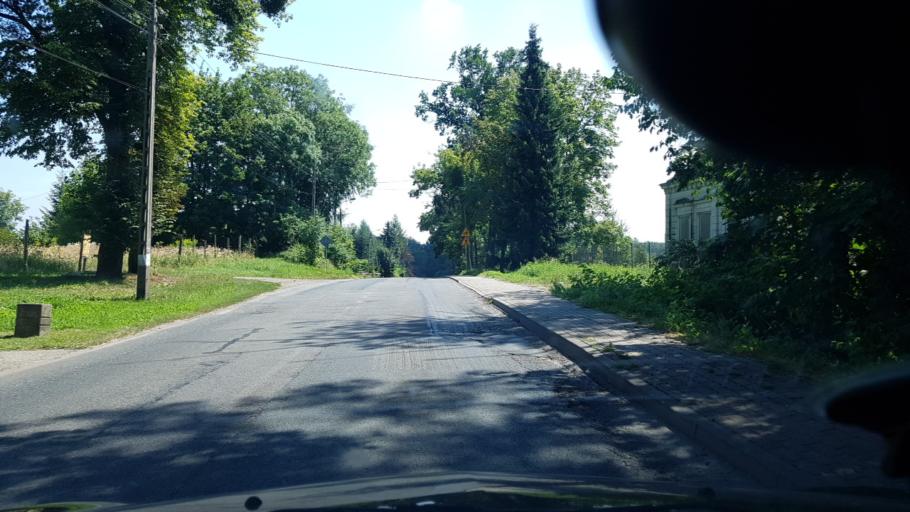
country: PL
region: Silesian Voivodeship
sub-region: Powiat wodzislawski
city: Marklowice
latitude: 50.0166
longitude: 18.5355
